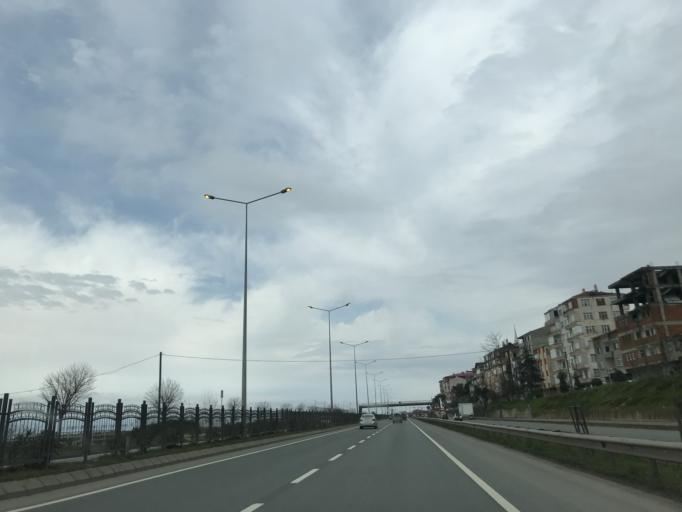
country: TR
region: Trabzon
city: Arsin
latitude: 40.9557
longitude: 39.9414
